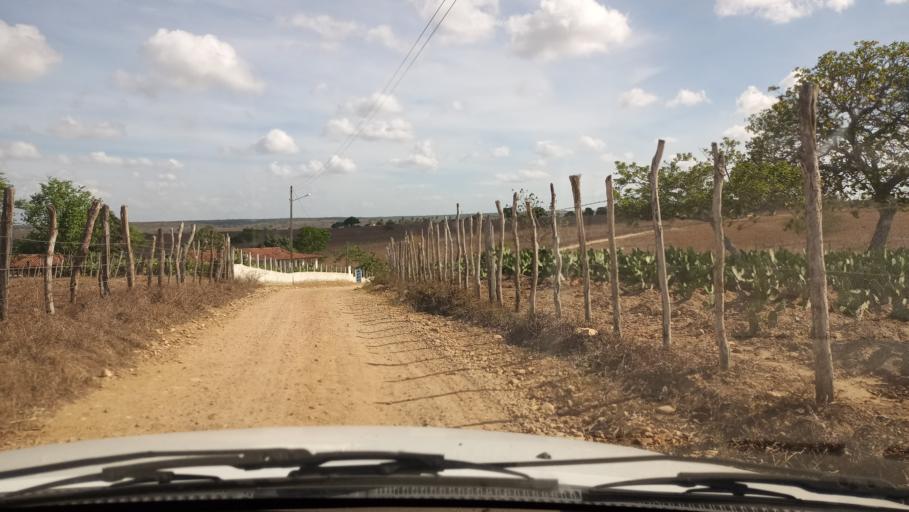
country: BR
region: Rio Grande do Norte
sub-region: Goianinha
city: Goianinha
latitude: -6.3123
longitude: -35.3070
